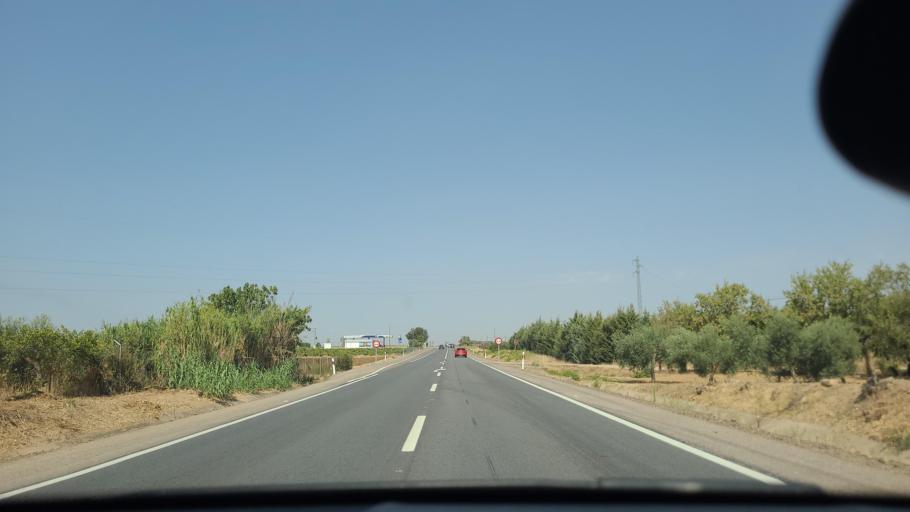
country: ES
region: Extremadura
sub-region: Provincia de Badajoz
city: Puebla de Sancho Perez
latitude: 38.4022
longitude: -6.3565
